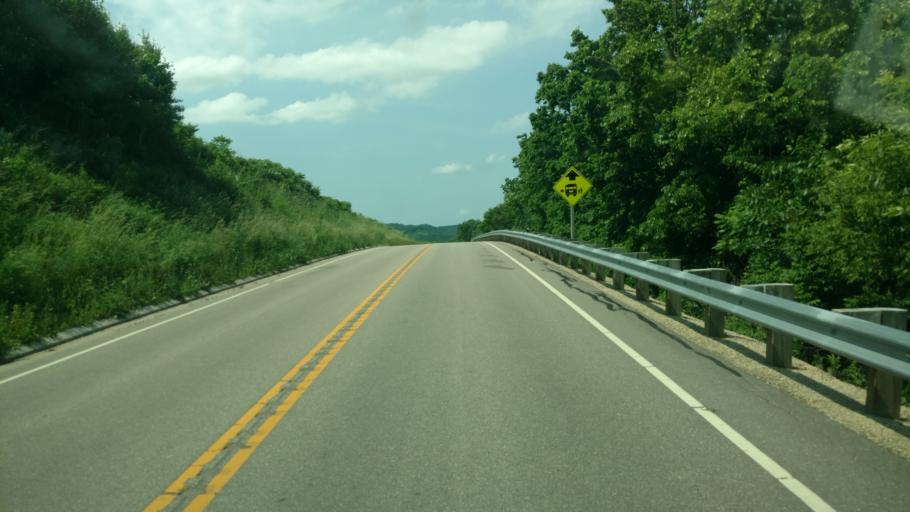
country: US
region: Wisconsin
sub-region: Vernon County
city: Westby
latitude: 43.5401
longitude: -90.6652
